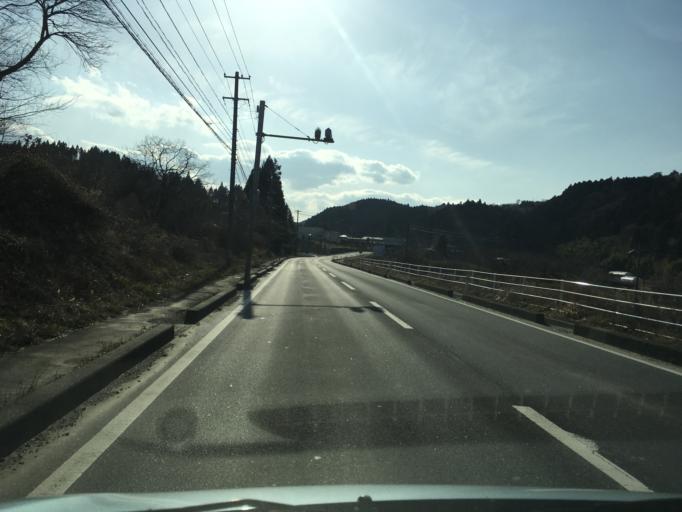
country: JP
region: Miyagi
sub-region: Oshika Gun
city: Onagawa Cho
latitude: 38.7789
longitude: 141.4517
